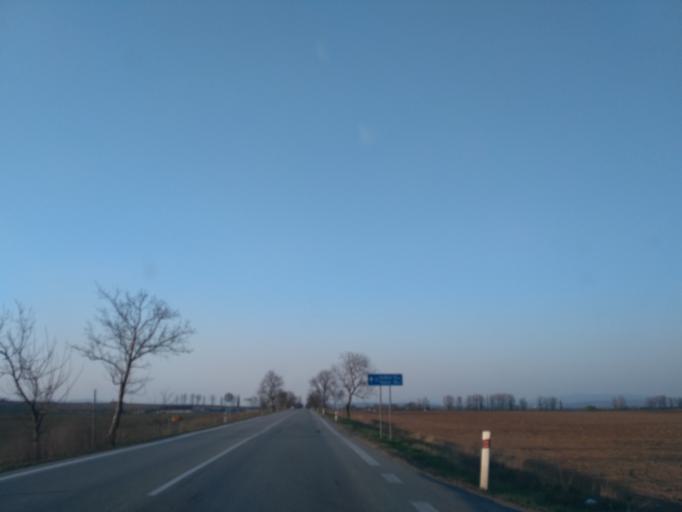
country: HU
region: Borsod-Abauj-Zemplen
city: Gonc
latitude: 48.5859
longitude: 21.2597
